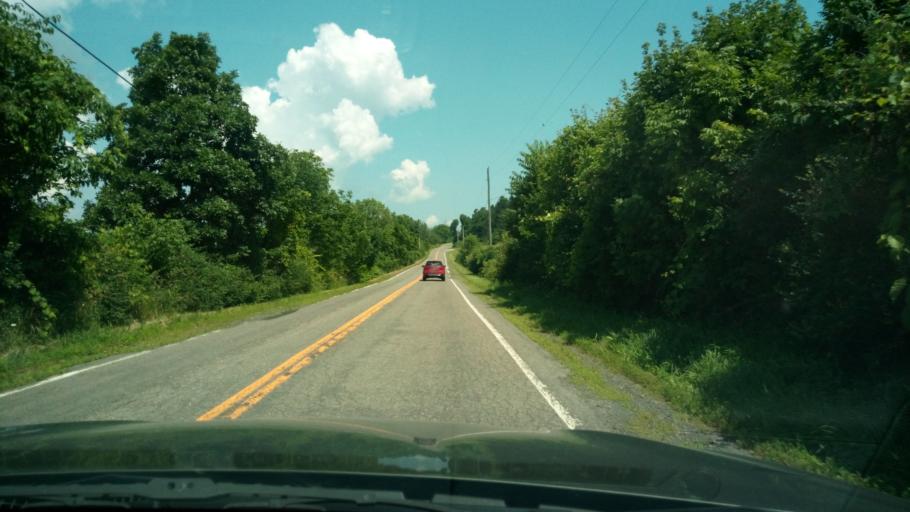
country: US
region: New York
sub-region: Chemung County
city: Horseheads North
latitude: 42.2572
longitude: -76.8013
